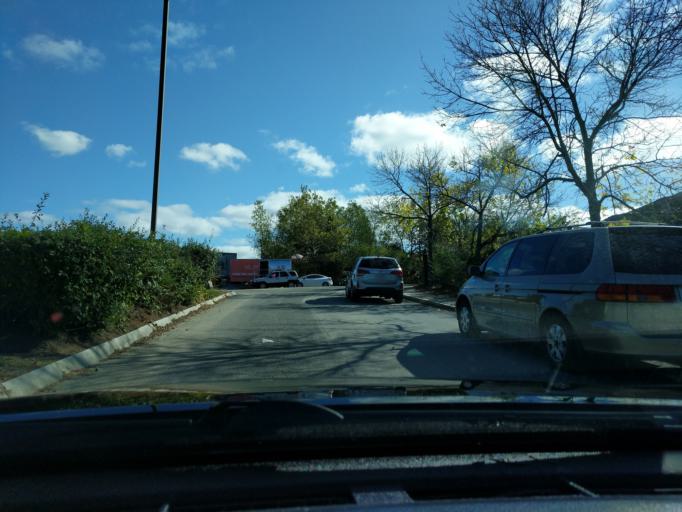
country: US
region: Massachusetts
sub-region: Norfolk County
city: Braintree
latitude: 42.2292
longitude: -71.0155
